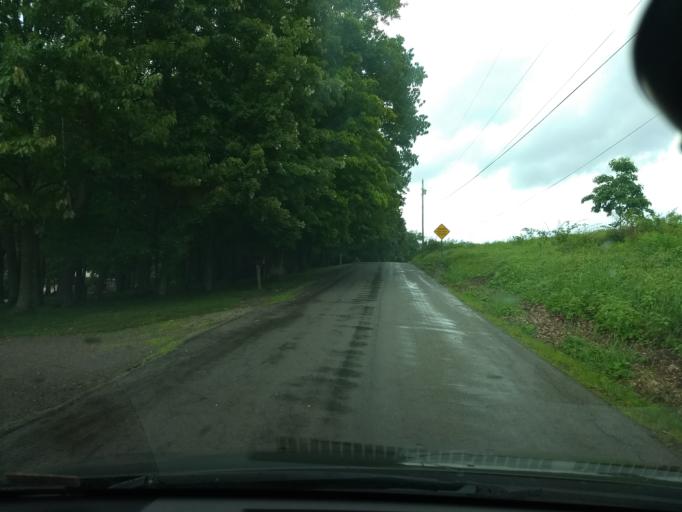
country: US
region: Pennsylvania
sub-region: Westmoreland County
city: Avonmore
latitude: 40.5407
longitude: -79.4945
